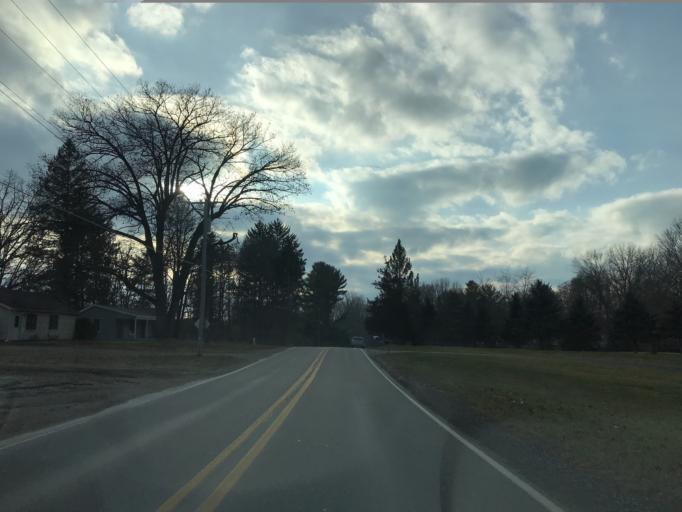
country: US
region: Michigan
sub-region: Livingston County
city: Whitmore Lake
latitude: 42.4676
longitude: -83.7032
